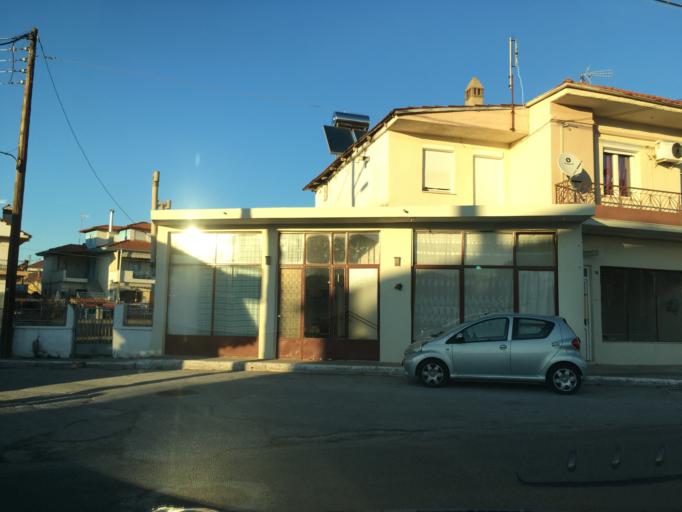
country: GR
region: West Macedonia
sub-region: Nomos Kozanis
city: Kozani
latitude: 40.2915
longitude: 21.7365
